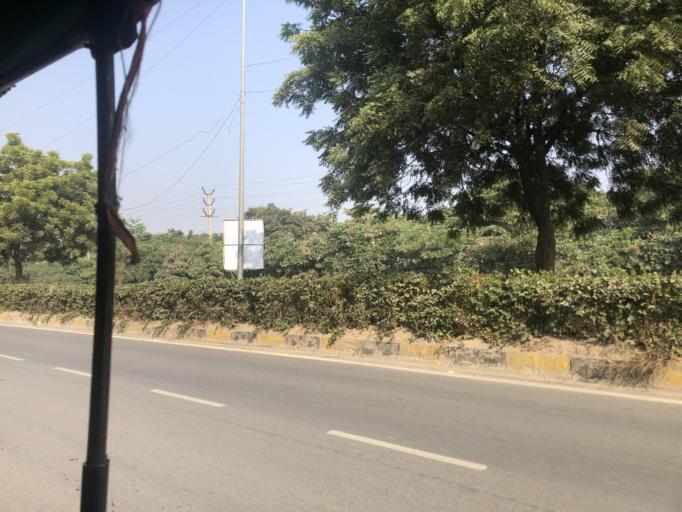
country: IN
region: Haryana
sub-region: Gurgaon
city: Gurgaon
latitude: 28.4445
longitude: 77.0825
